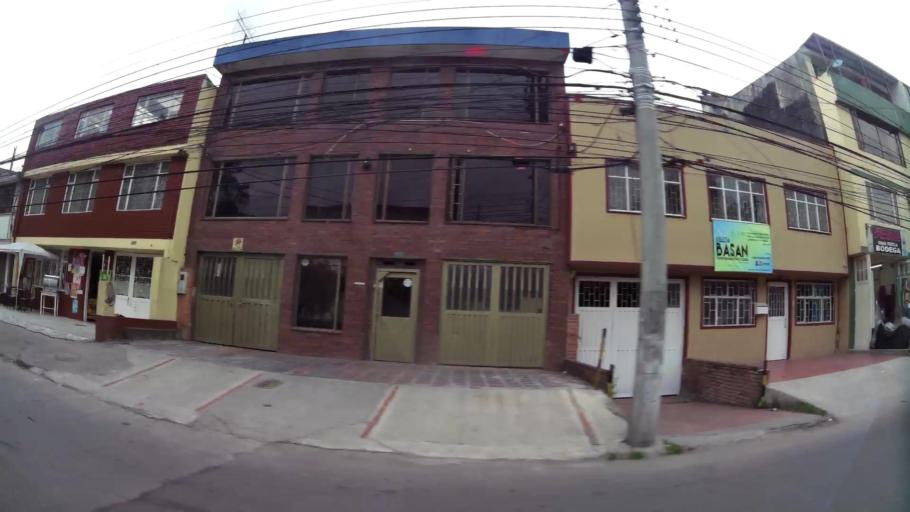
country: CO
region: Bogota D.C.
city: Bogota
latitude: 4.6738
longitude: -74.1194
